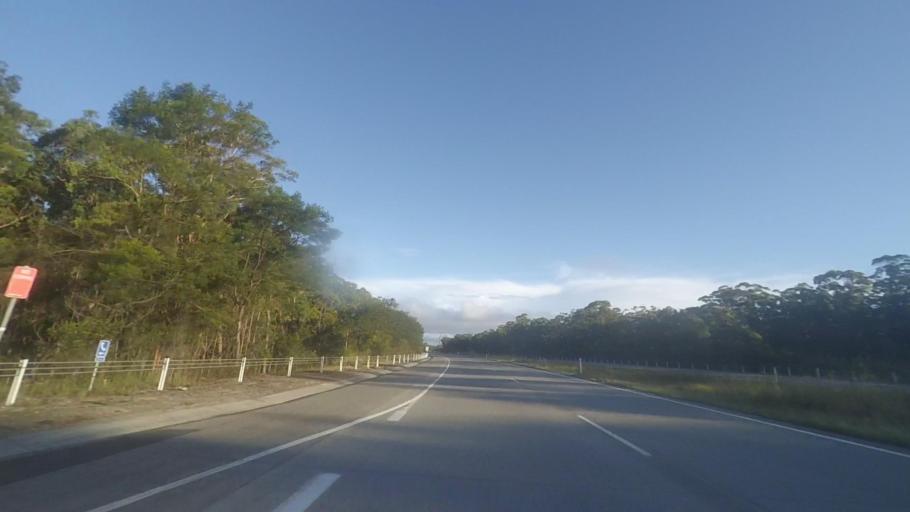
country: AU
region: New South Wales
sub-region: Great Lakes
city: Bulahdelah
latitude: -32.4864
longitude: 152.1948
